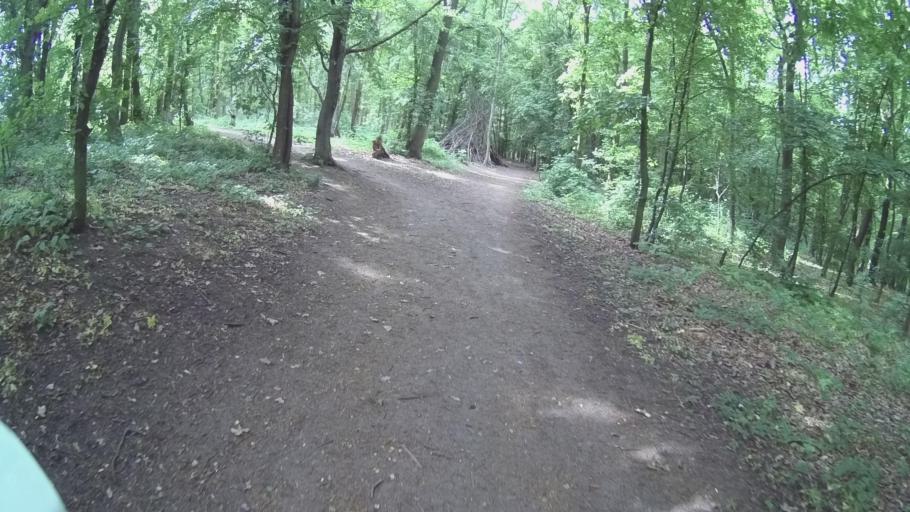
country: CZ
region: Central Bohemia
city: Libeznice
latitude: 50.1732
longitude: 14.4764
